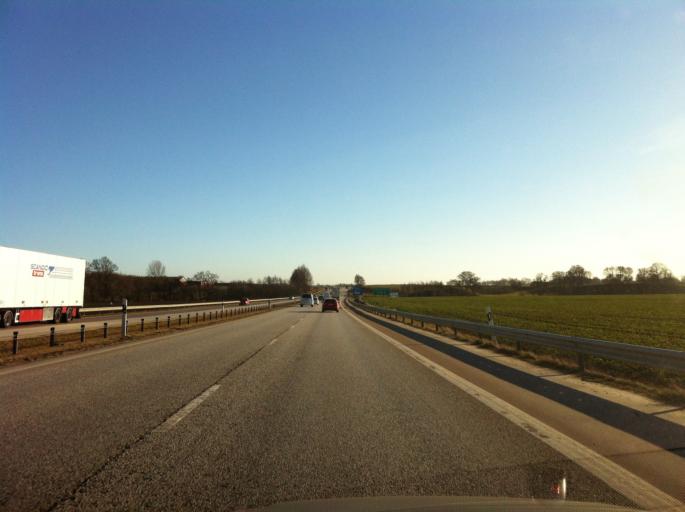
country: SE
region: Skane
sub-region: Angelholms Kommun
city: AEngelholm
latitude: 56.2384
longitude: 12.8988
